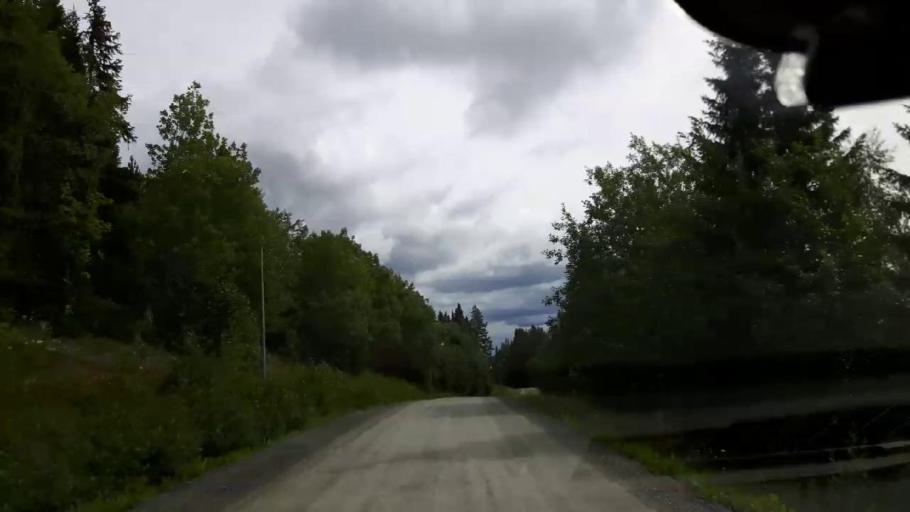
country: SE
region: Jaemtland
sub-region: Krokoms Kommun
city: Valla
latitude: 63.6222
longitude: 14.0562
